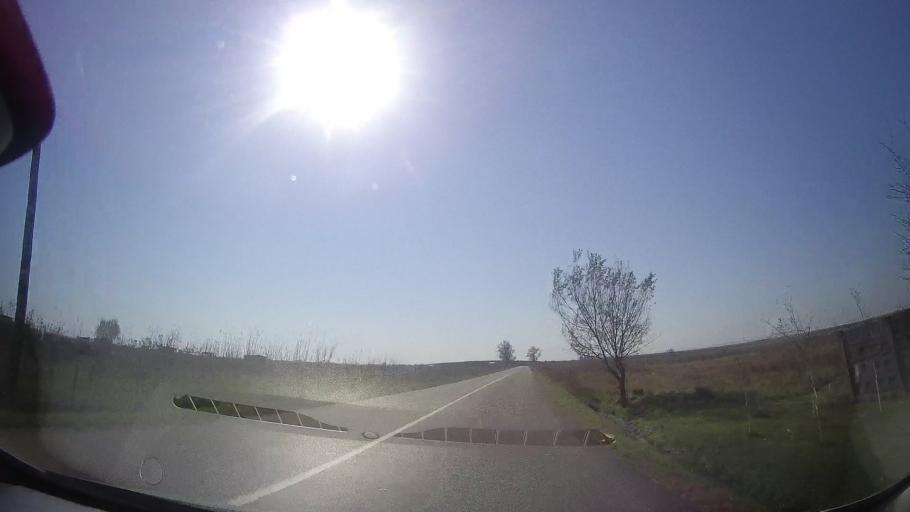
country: RO
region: Timis
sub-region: Comuna Ghizela
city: Ghizela
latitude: 45.7897
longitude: 21.7304
